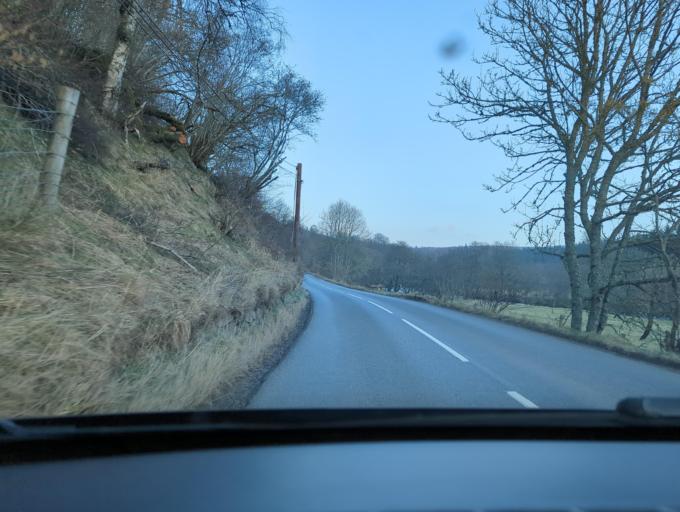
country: GB
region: Scotland
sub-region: Perth and Kinross
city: Methven
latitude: 56.5377
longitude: -3.6866
